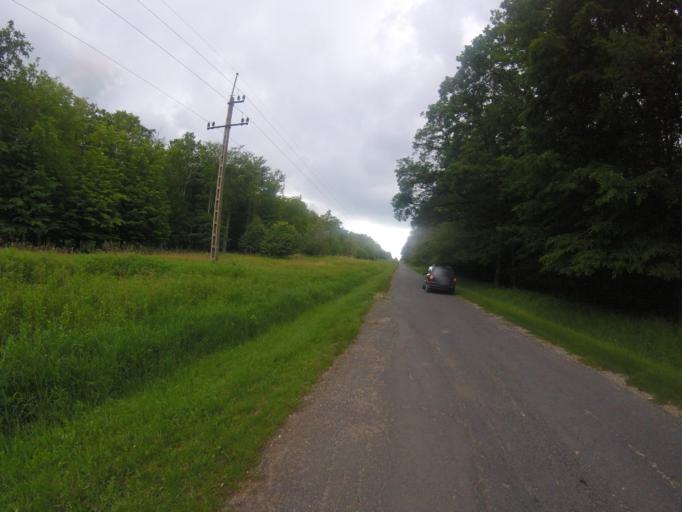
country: HU
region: Veszprem
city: Urkut
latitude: 47.0552
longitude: 17.6614
